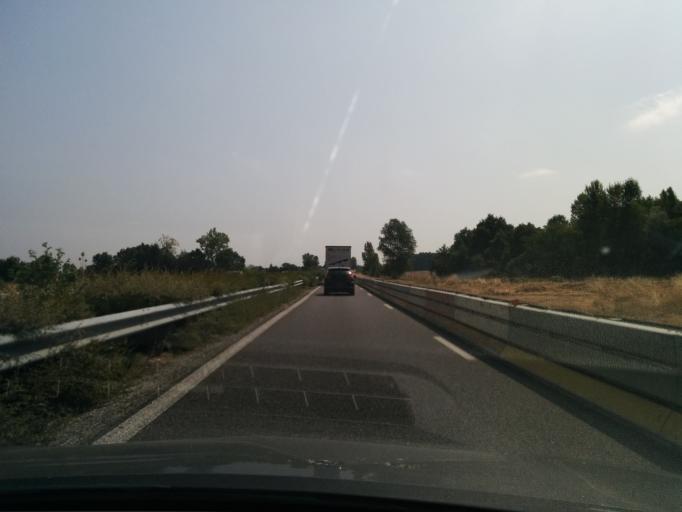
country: FR
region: Midi-Pyrenees
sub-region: Departement du Tarn
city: Saint-Sulpice-la-Pointe
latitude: 43.7542
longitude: 1.6603
